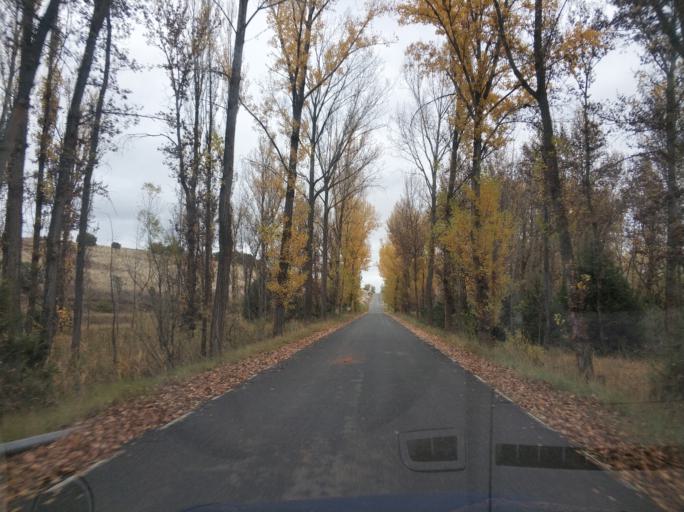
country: ES
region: Castille and Leon
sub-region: Provincia de Soria
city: San Esteban de Gormaz
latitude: 41.5869
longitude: -3.1879
